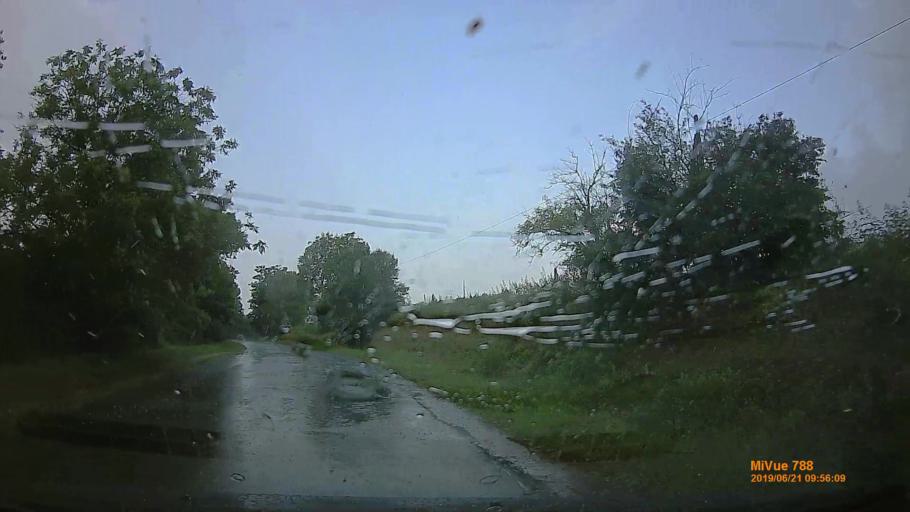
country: HU
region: Baranya
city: Buekkoesd
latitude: 46.2267
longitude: 17.9829
